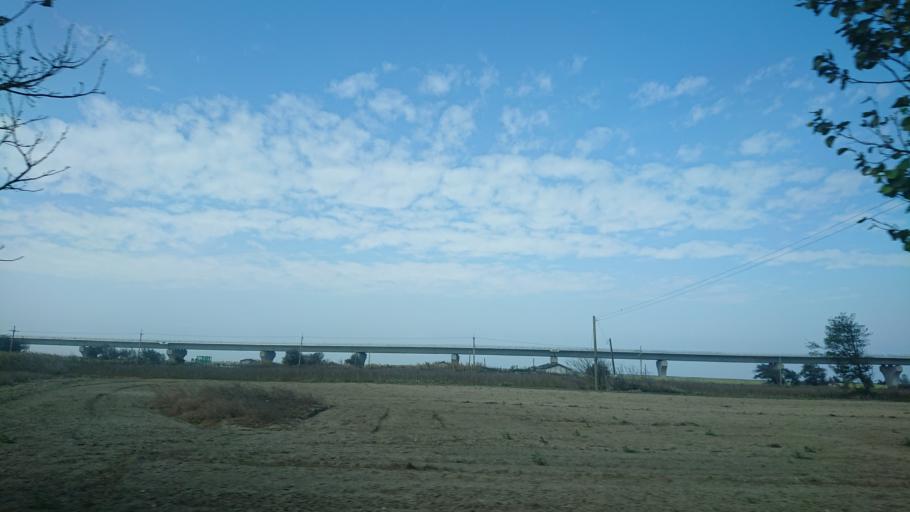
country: TW
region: Taiwan
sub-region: Changhua
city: Chang-hua
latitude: 23.9092
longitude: 120.3096
